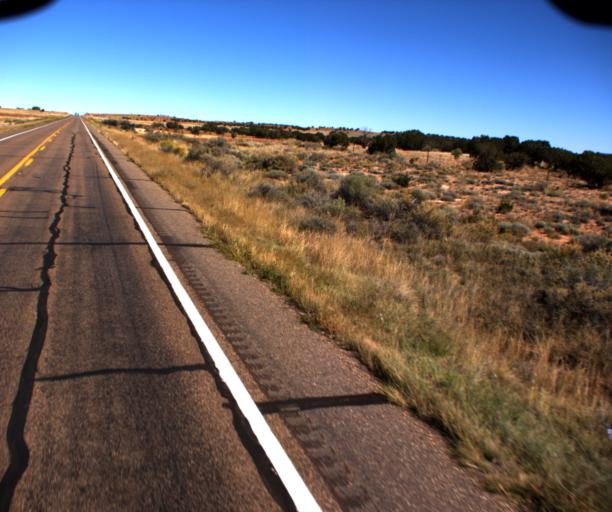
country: US
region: Arizona
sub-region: Apache County
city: Saint Johns
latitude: 34.4544
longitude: -109.4060
